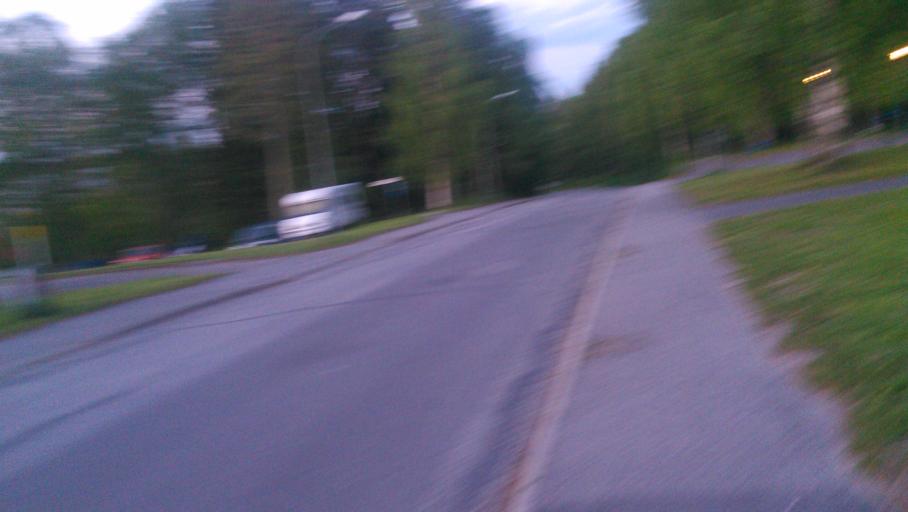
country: SE
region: Vaesterbotten
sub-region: Umea Kommun
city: Umea
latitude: 63.8275
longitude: 20.3051
